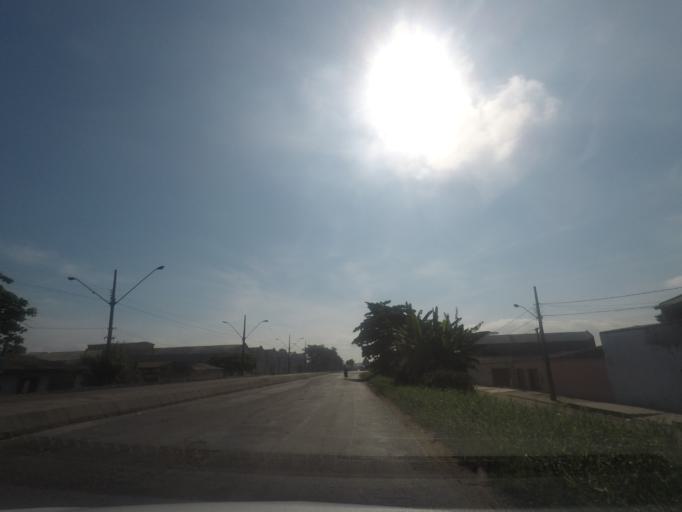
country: BR
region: Parana
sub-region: Paranagua
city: Paranagua
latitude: -25.5178
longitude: -48.5240
